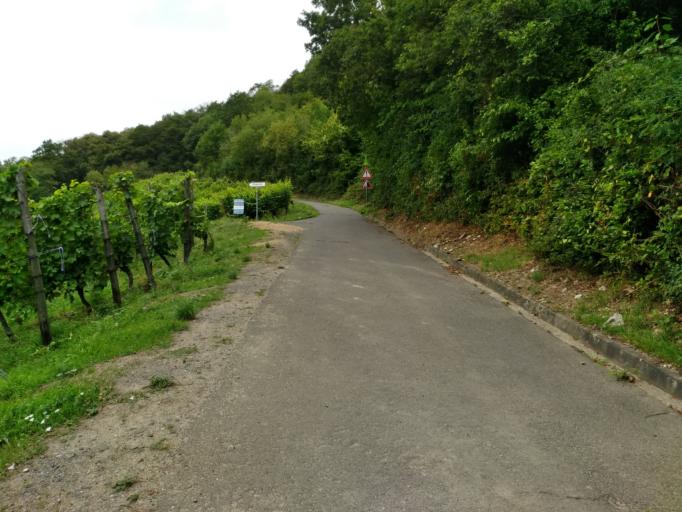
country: DE
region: North Rhine-Westphalia
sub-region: Regierungsbezirk Koln
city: Konigswinter
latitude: 50.6650
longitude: 7.2052
